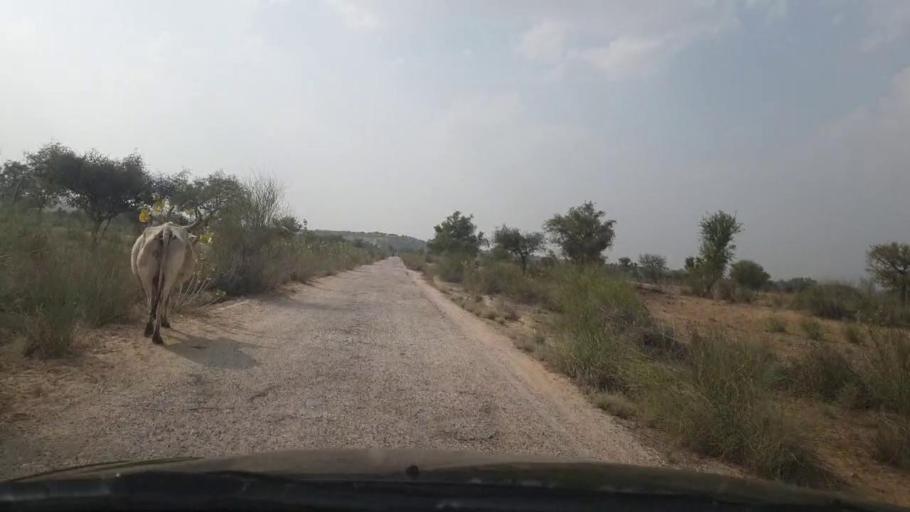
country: PK
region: Sindh
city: Islamkot
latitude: 24.9651
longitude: 70.6237
